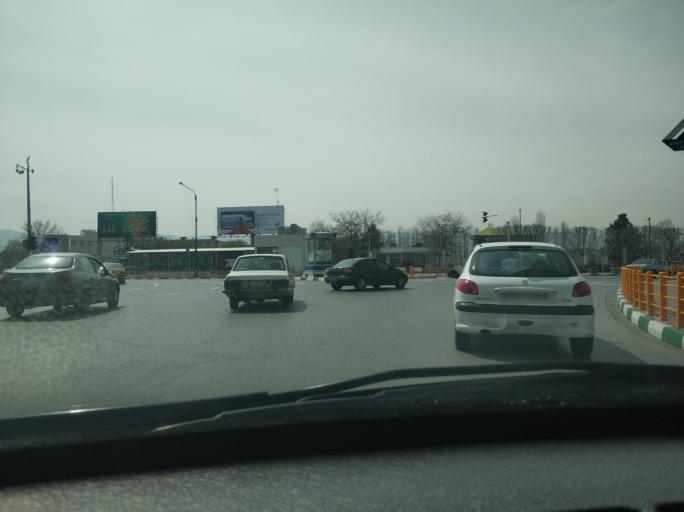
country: IR
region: Razavi Khorasan
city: Mashhad
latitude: 36.3006
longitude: 59.5633
